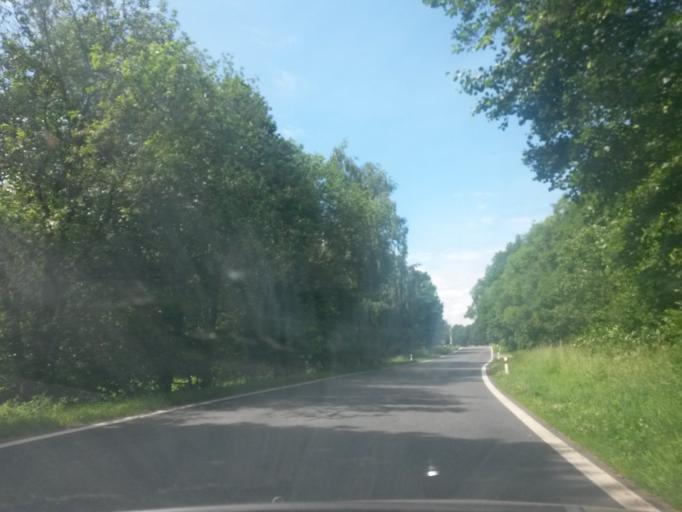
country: CZ
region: Vysocina
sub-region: Okres Zd'ar nad Sazavou
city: Jimramov
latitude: 49.6078
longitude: 16.1646
